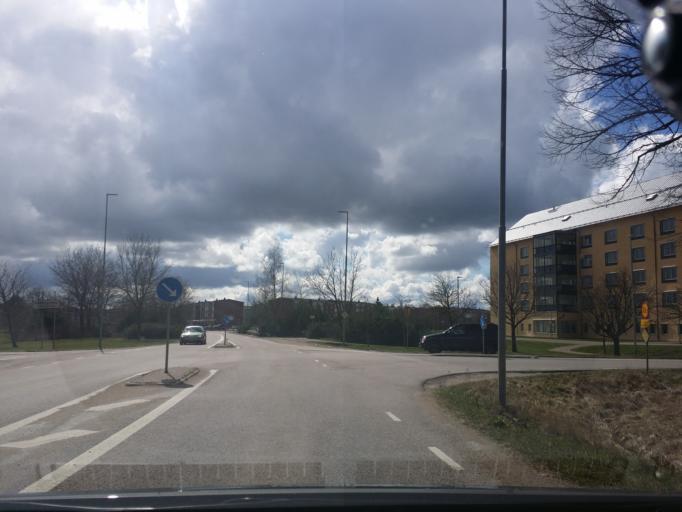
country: SE
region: Vaestmanland
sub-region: Sala Kommun
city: Sala
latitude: 59.9278
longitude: 16.5908
